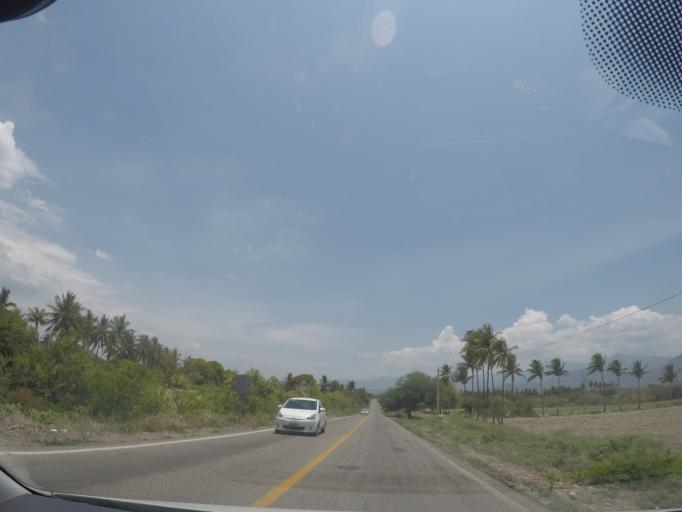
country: MX
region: Oaxaca
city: Santa Maria Jalapa del Marques
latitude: 16.4393
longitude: -95.5114
